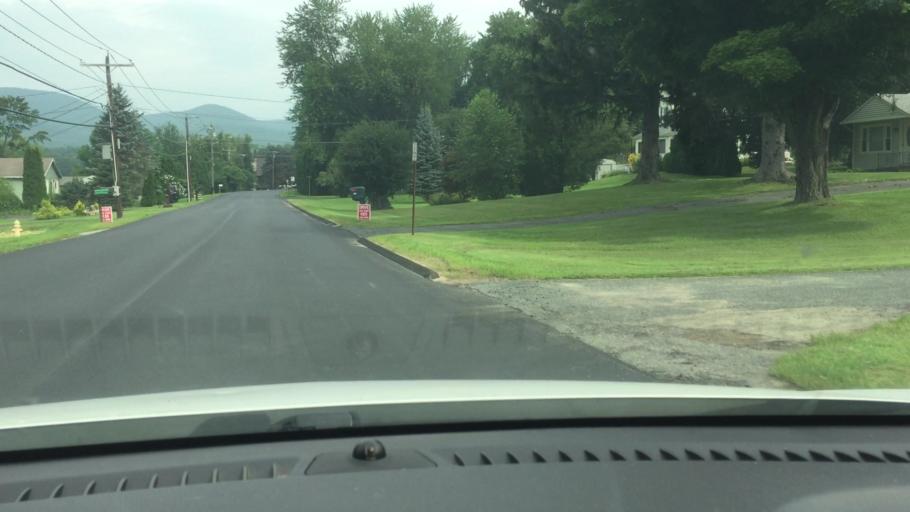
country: US
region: Massachusetts
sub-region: Berkshire County
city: Pittsfield
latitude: 42.4819
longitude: -73.2726
